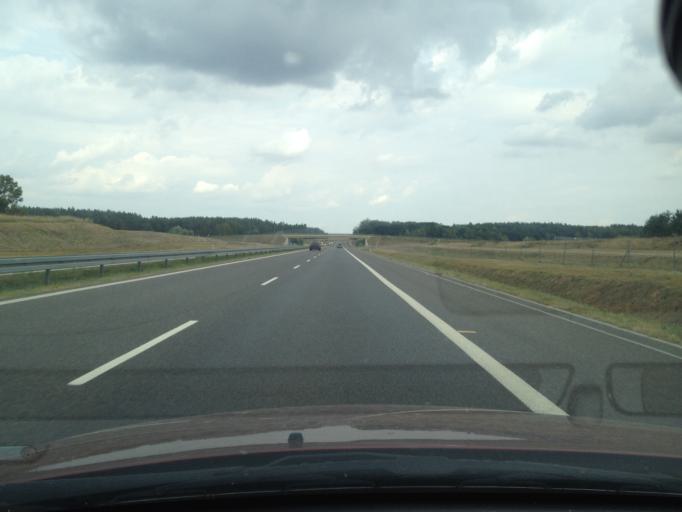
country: PL
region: West Pomeranian Voivodeship
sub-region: Powiat mysliborski
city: Mysliborz
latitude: 53.0036
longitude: 14.8620
